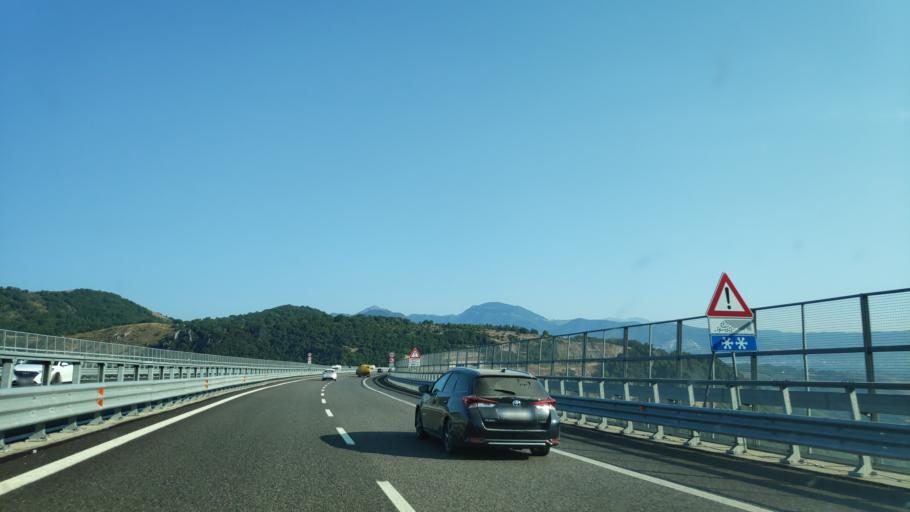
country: IT
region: Calabria
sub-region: Provincia di Cosenza
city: Laino Castello-Nuovo Centro
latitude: 39.9341
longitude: 15.9612
